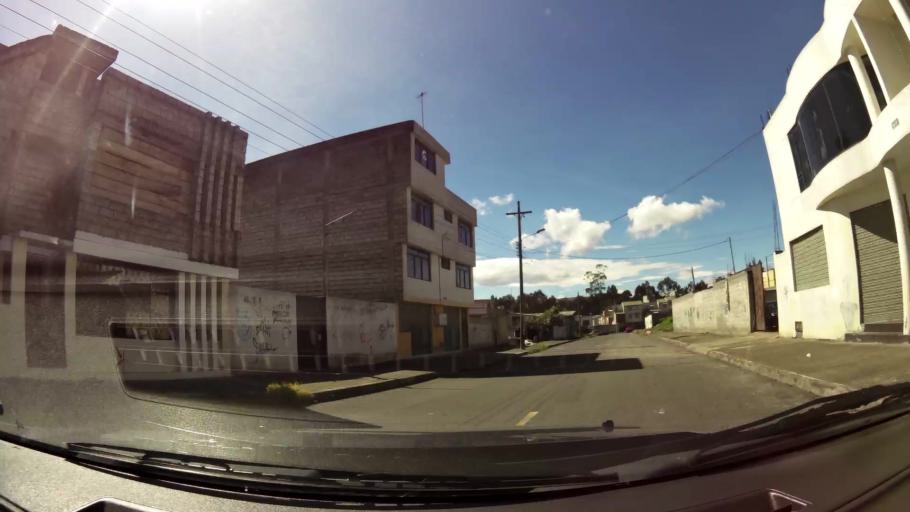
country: EC
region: Pichincha
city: Quito
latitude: -0.2872
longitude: -78.5588
